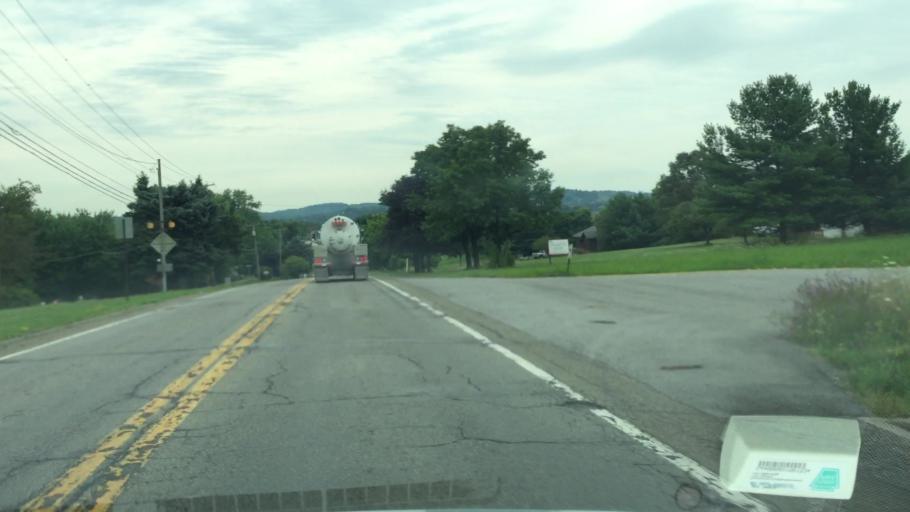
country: US
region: Pennsylvania
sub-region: Butler County
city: Mars
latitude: 40.6944
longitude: -79.9740
